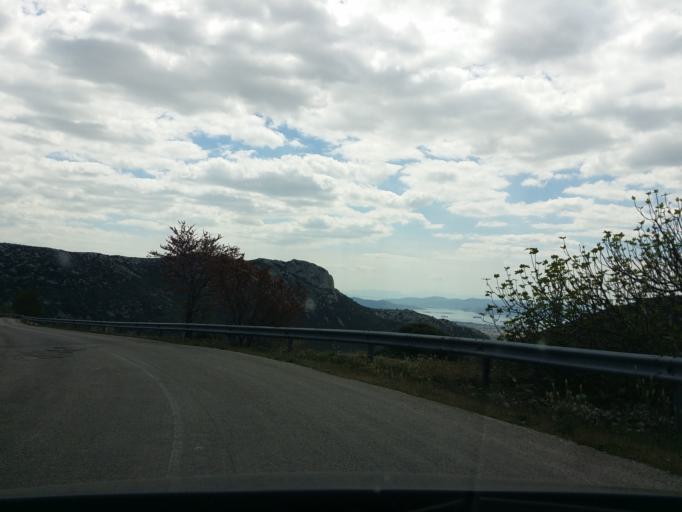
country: GR
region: Attica
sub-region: Nomarchia Dytikis Attikis
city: Fyli
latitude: 38.1151
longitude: 23.6472
